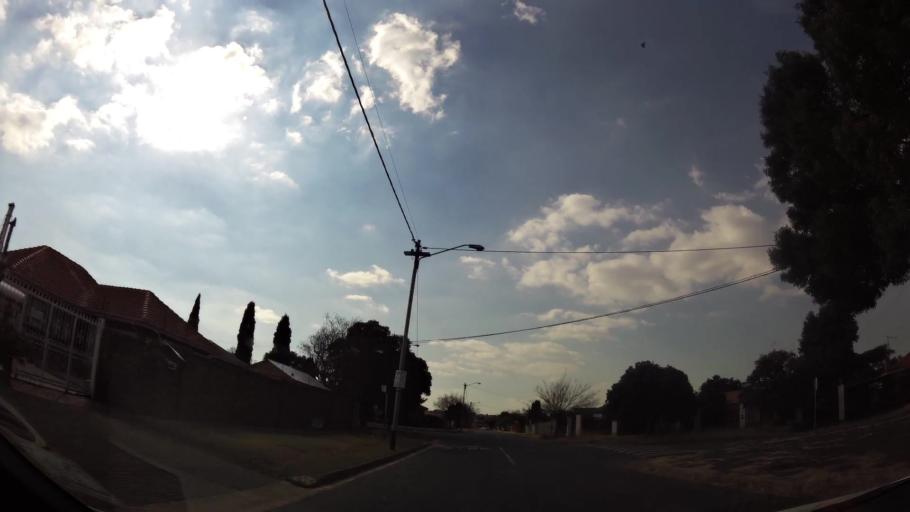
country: ZA
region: Gauteng
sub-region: Ekurhuleni Metropolitan Municipality
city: Germiston
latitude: -26.1720
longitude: 28.1732
